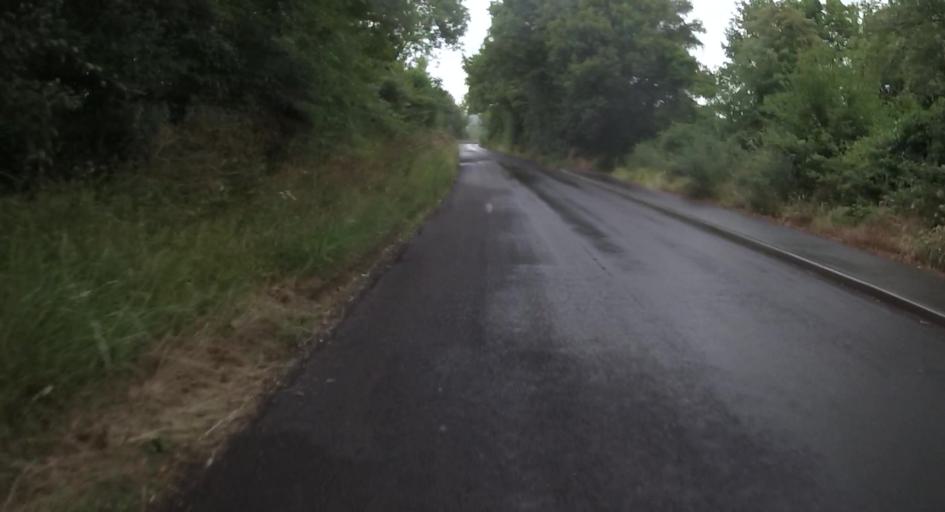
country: GB
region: England
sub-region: Hampshire
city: Odiham
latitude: 51.2500
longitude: -0.9531
